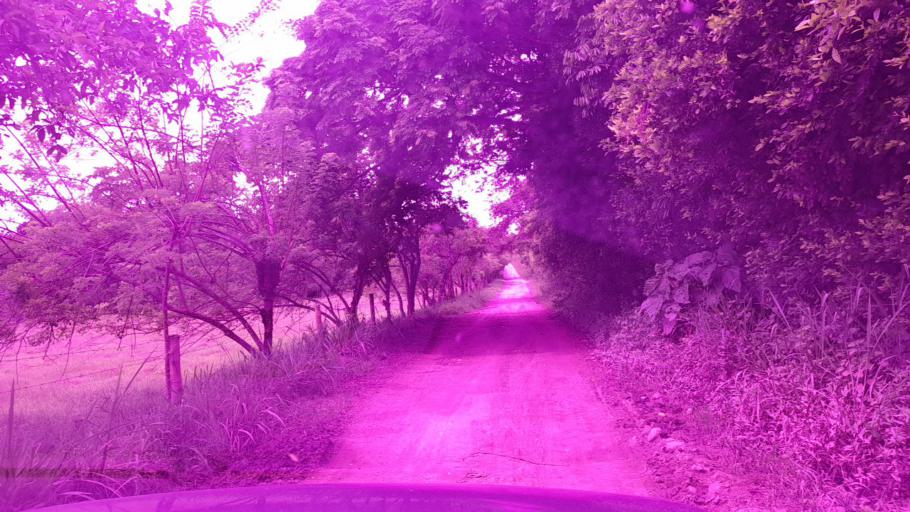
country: CO
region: Valle del Cauca
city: Andalucia
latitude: 4.1669
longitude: -76.0890
